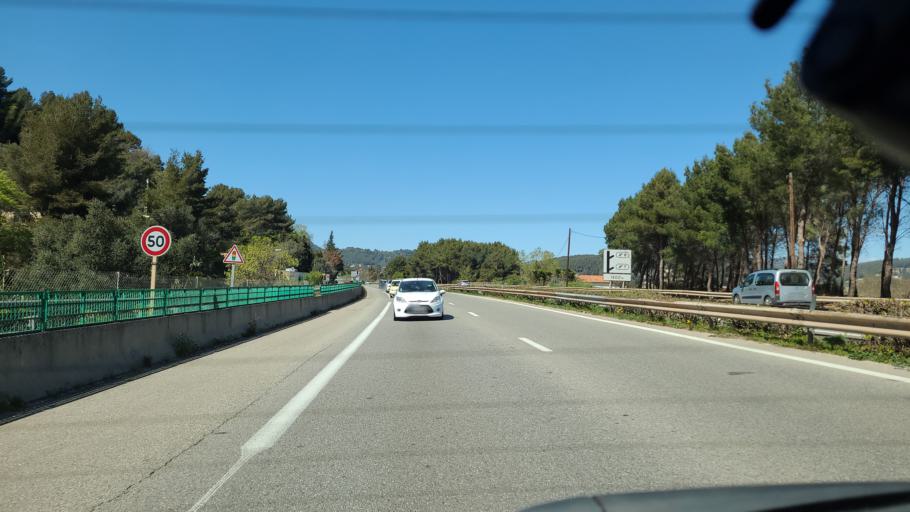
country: FR
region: Provence-Alpes-Cote d'Azur
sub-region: Departement du Var
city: Sollies-Ville
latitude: 43.1828
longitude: 6.0441
